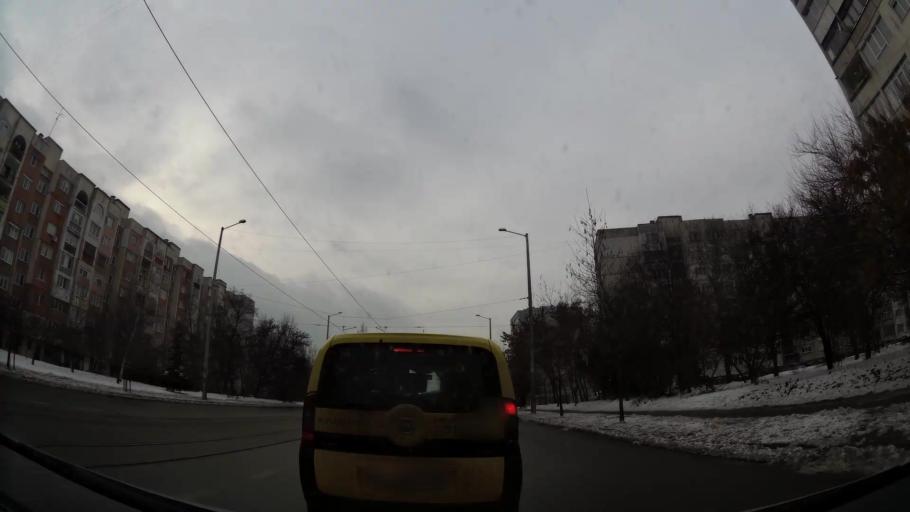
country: BG
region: Sofia-Capital
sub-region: Stolichna Obshtina
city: Sofia
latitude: 42.7096
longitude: 23.2999
